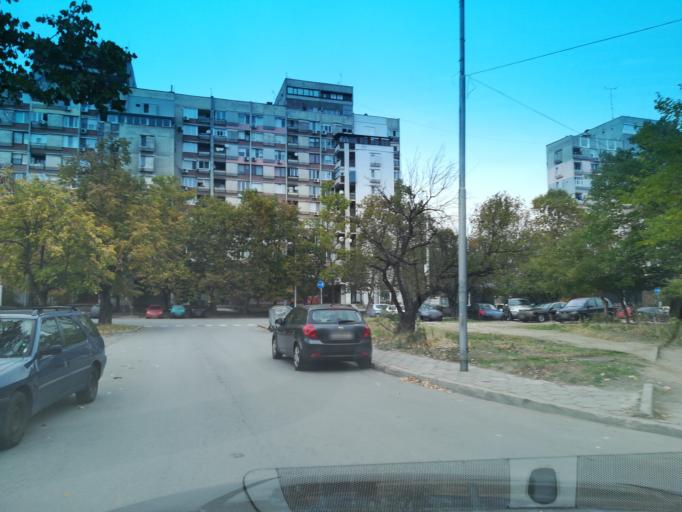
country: BG
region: Plovdiv
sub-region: Obshtina Plovdiv
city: Plovdiv
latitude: 42.1394
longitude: 24.7937
